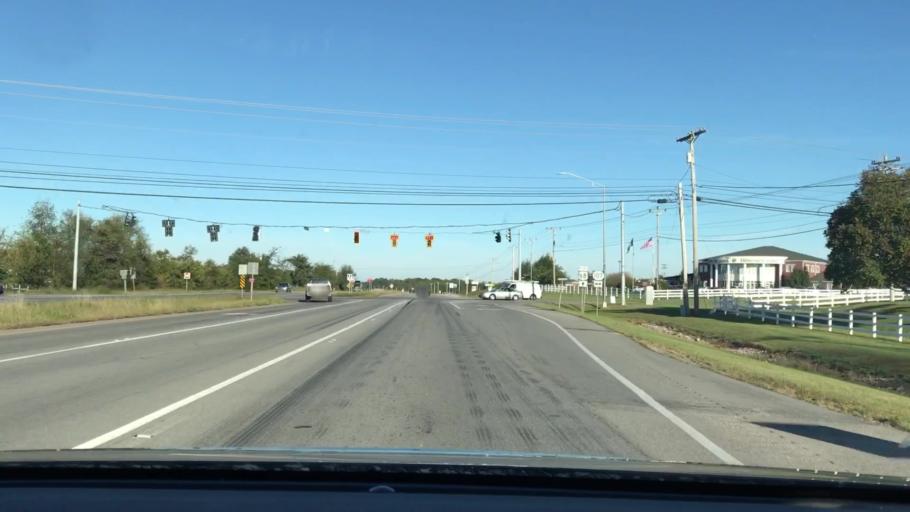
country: US
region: Kentucky
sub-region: Christian County
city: Hopkinsville
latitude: 36.8214
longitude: -87.5040
